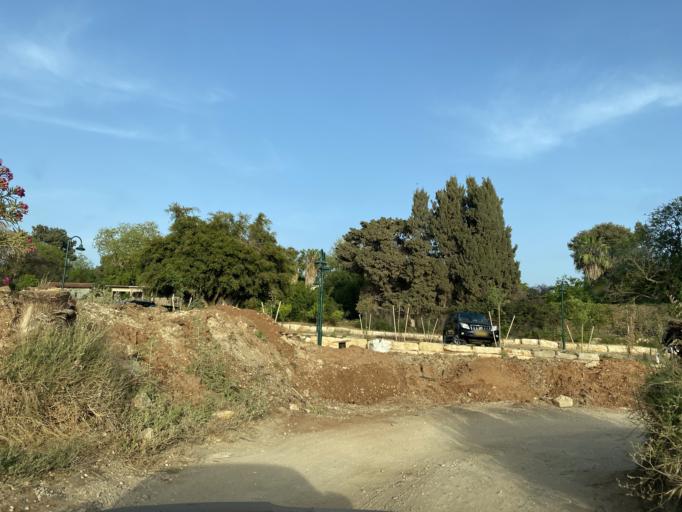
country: IL
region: Tel Aviv
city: Herzliyya
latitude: 32.1580
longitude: 34.8285
